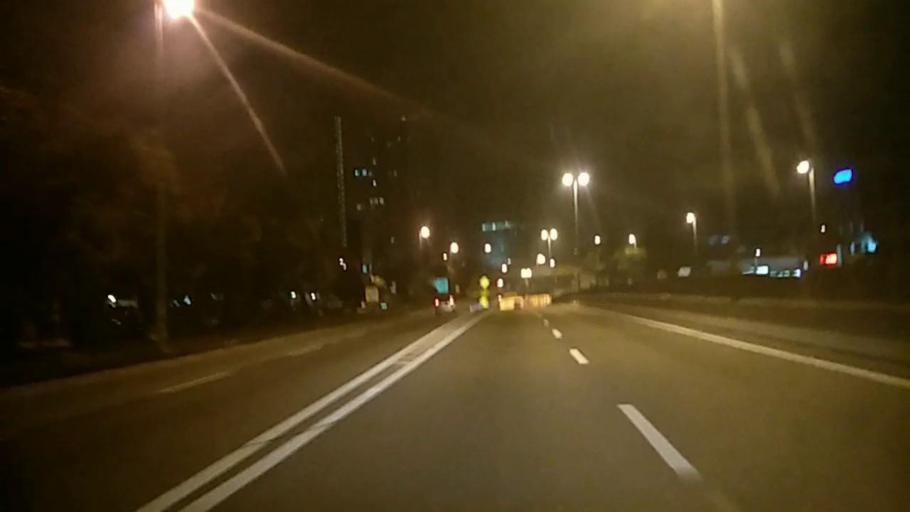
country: MY
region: Selangor
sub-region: Petaling
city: Petaling Jaya
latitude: 3.1348
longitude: 101.6247
